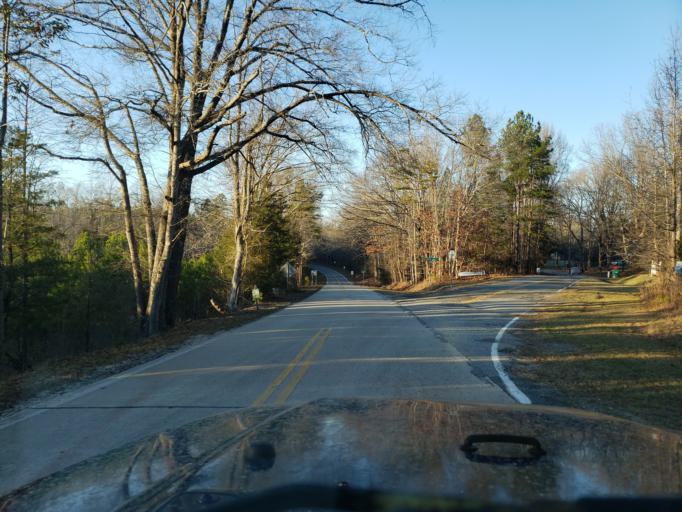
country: US
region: South Carolina
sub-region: Cherokee County
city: Blacksburg
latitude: 35.0457
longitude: -81.4132
